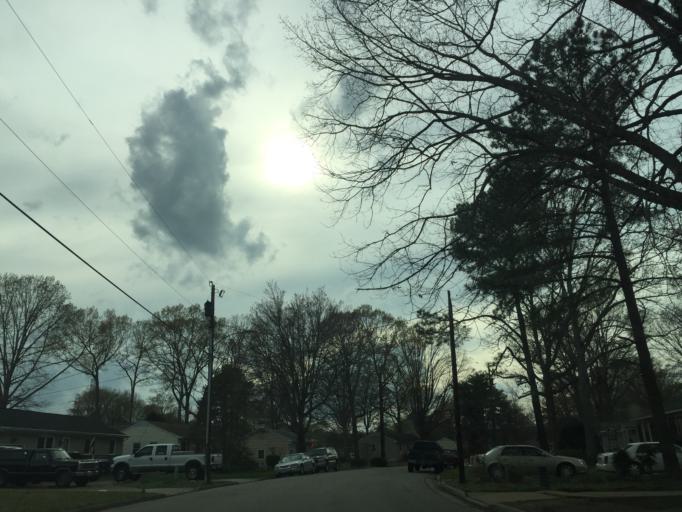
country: US
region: Virginia
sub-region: City of Newport News
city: Newport News
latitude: 37.0775
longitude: -76.4529
